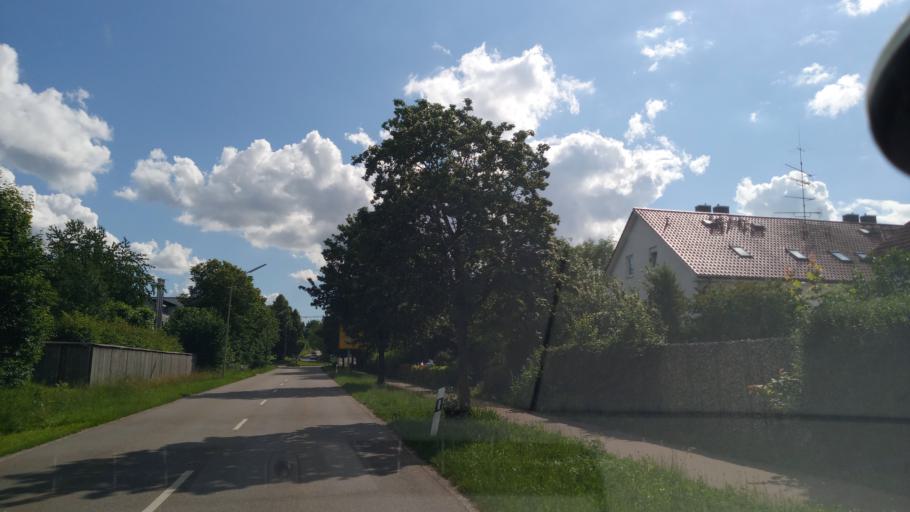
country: DE
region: Bavaria
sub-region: Upper Bavaria
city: Vierkirchen
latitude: 48.3587
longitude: 11.4406
